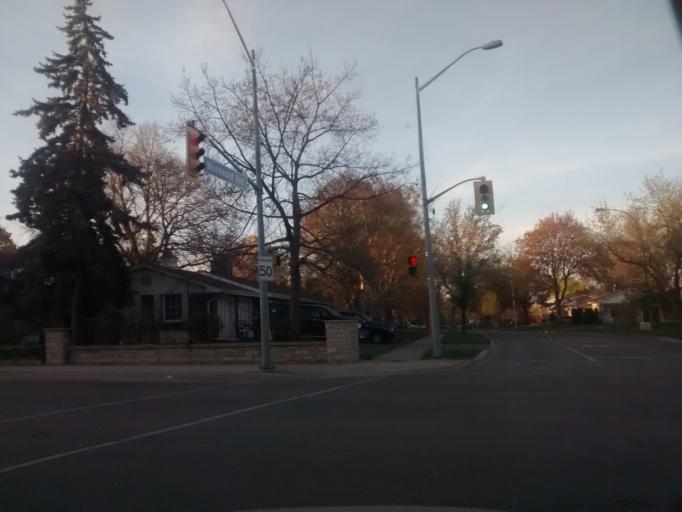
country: CA
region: Ontario
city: Burlington
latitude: 43.3424
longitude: -79.7910
